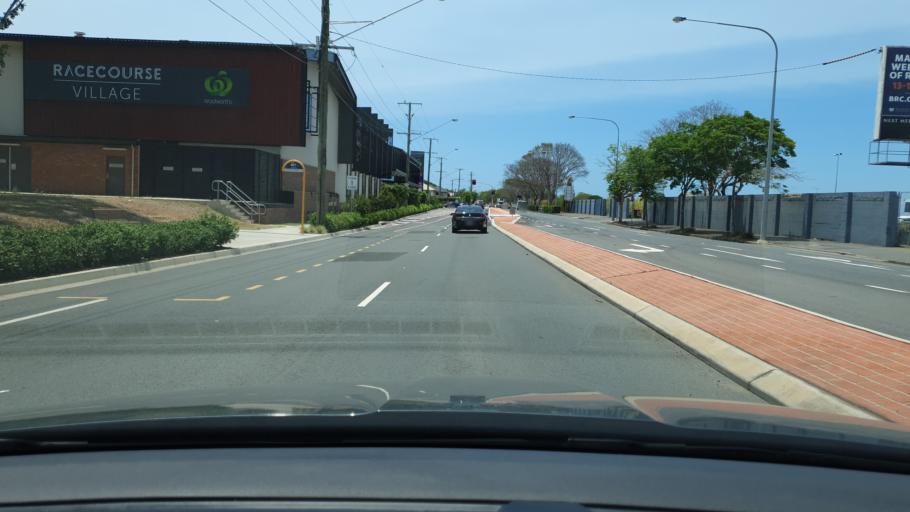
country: AU
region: Queensland
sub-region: Brisbane
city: Ascot
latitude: -27.4281
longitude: 153.0722
